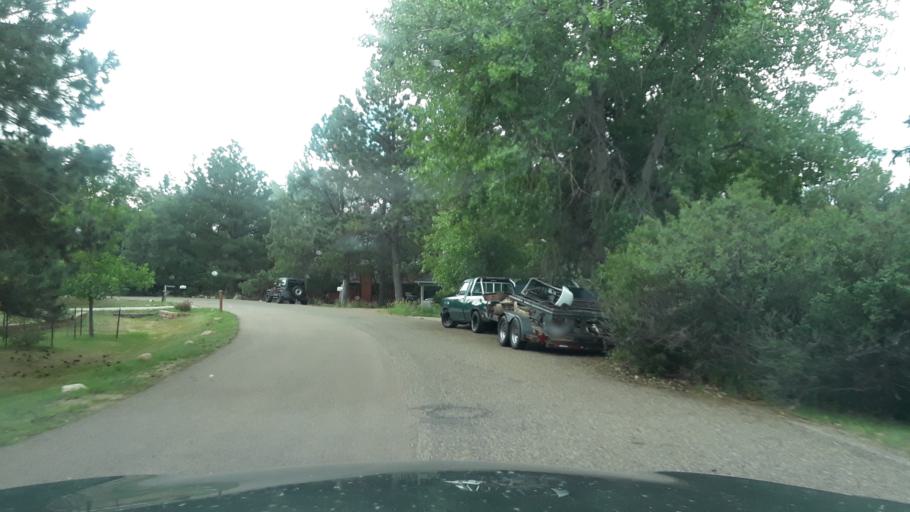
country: US
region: Colorado
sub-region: El Paso County
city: Air Force Academy
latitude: 38.9465
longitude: -104.8257
